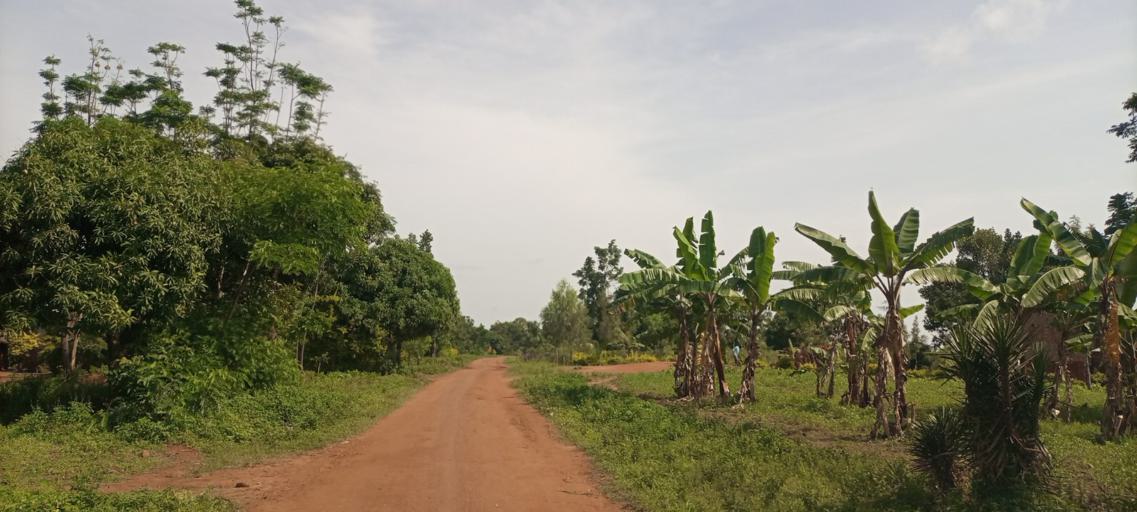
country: UG
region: Eastern Region
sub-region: Mbale District
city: Mbale
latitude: 1.1281
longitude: 34.0258
